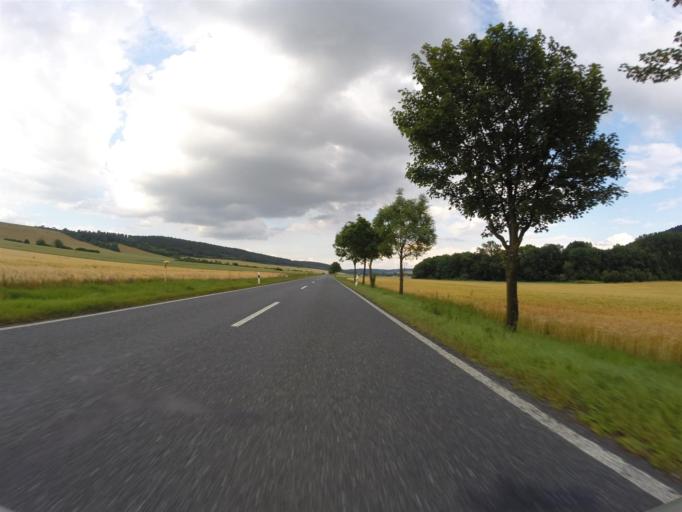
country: DE
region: Thuringia
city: Stadtilm
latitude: 50.7867
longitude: 11.1041
